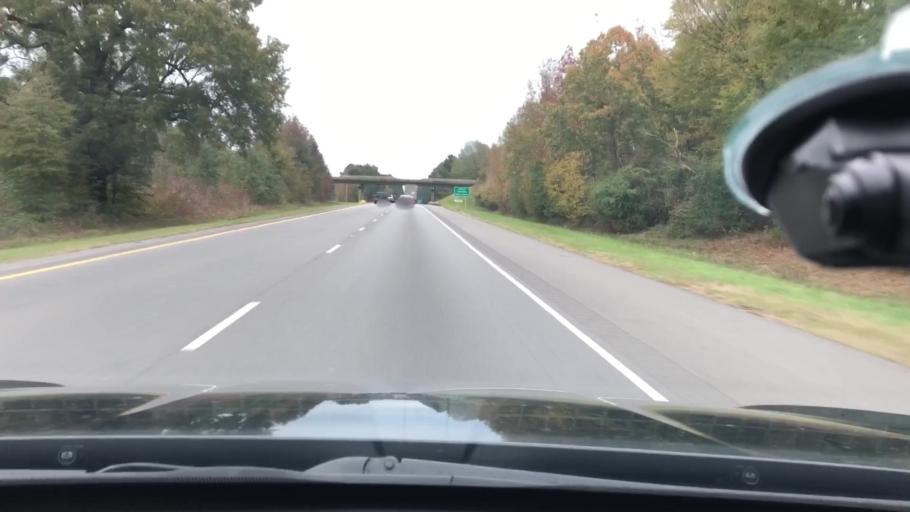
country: US
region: Arkansas
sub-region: Hempstead County
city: Hope
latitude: 33.6461
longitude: -93.6821
